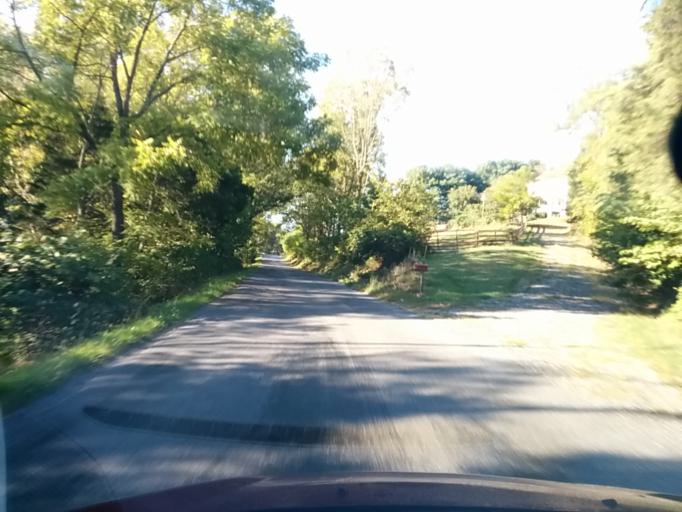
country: US
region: Virginia
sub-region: City of Lexington
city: Lexington
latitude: 37.7479
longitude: -79.5634
